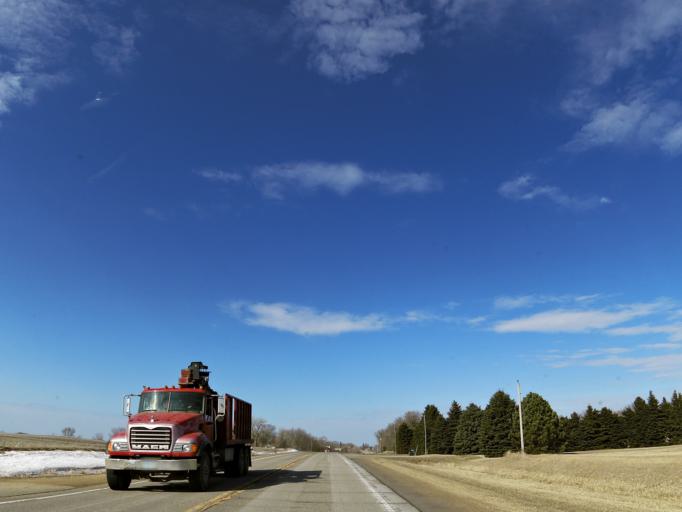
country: US
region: Minnesota
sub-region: Waseca County
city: Waseca
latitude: 44.1564
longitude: -93.5074
